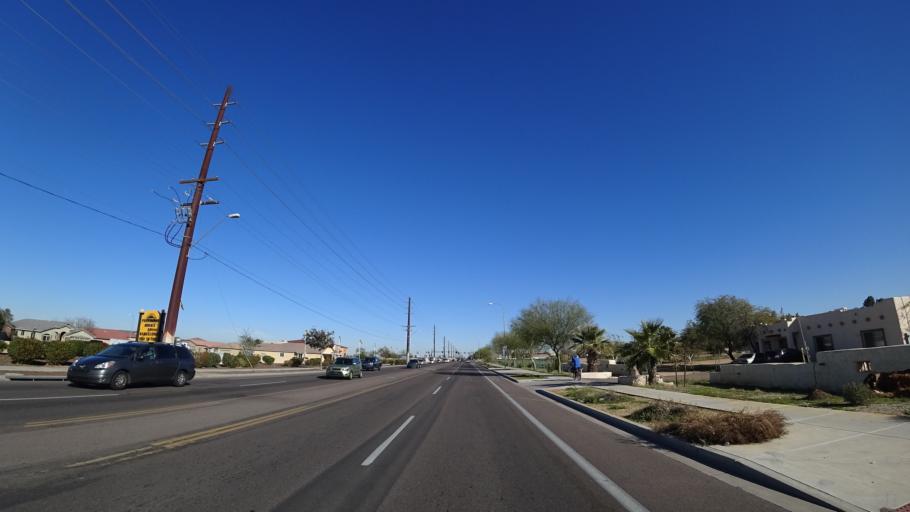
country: US
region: Arizona
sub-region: Maricopa County
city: Laveen
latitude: 33.3921
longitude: -112.1193
